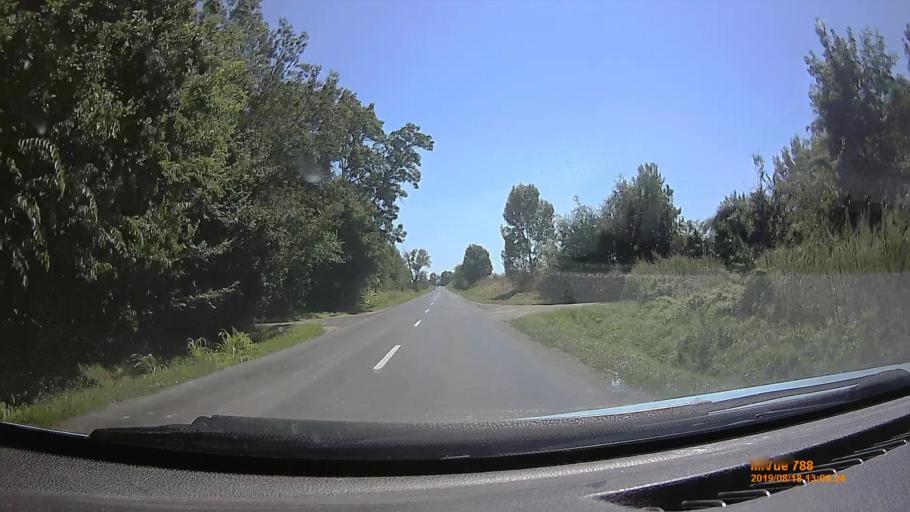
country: HU
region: Fejer
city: Kaloz
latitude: 46.9272
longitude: 18.5101
